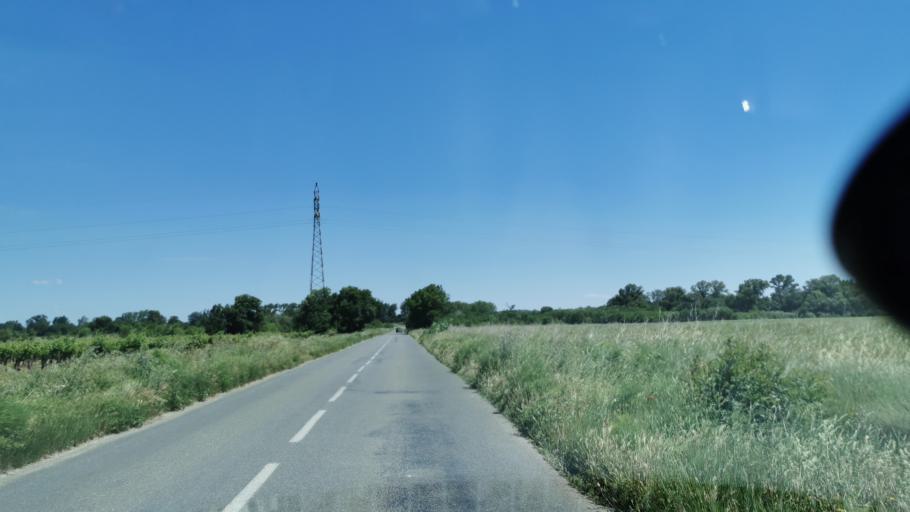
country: FR
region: Languedoc-Roussillon
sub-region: Departement de l'Aude
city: Saint-Marcel-sur-Aude
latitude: 43.2532
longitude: 2.9327
